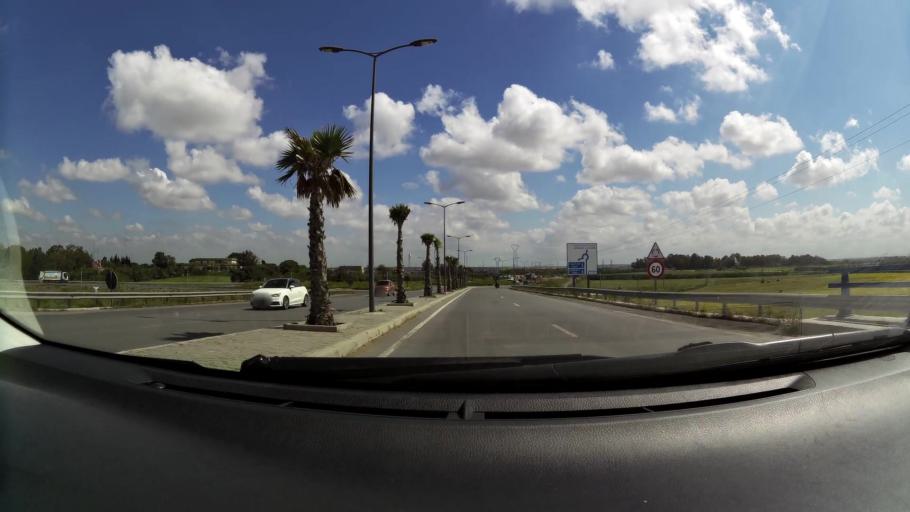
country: MA
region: Grand Casablanca
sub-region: Nouaceur
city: Bouskoura
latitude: 33.5088
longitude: -7.6117
